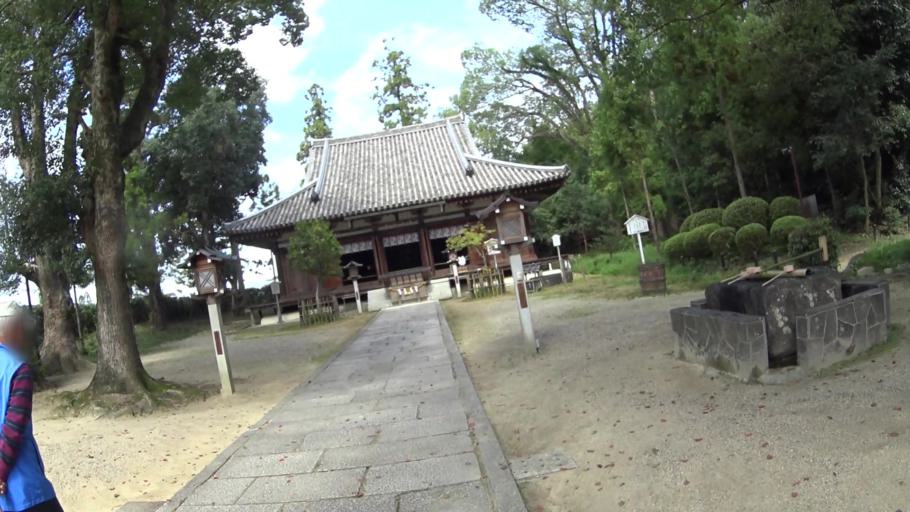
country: JP
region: Nara
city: Sakurai
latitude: 34.5302
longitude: 135.8503
